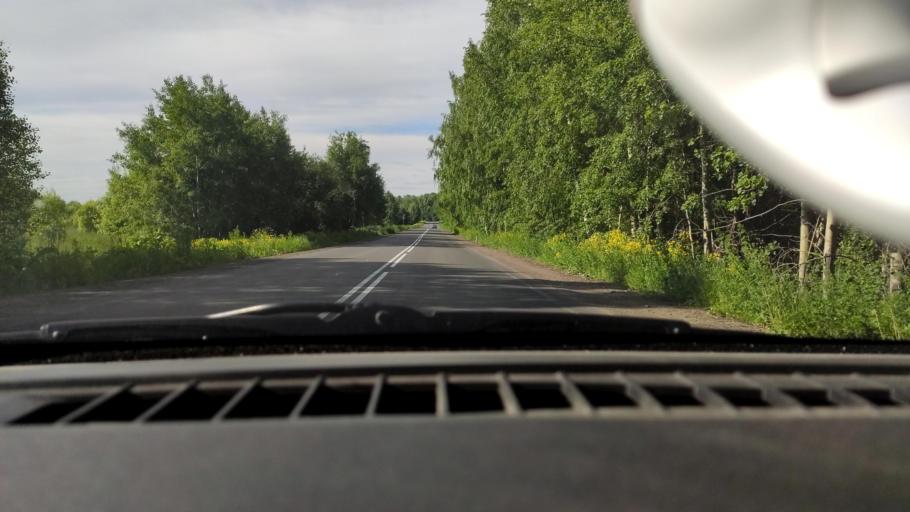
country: RU
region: Perm
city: Nytva
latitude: 57.9287
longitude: 55.4497
